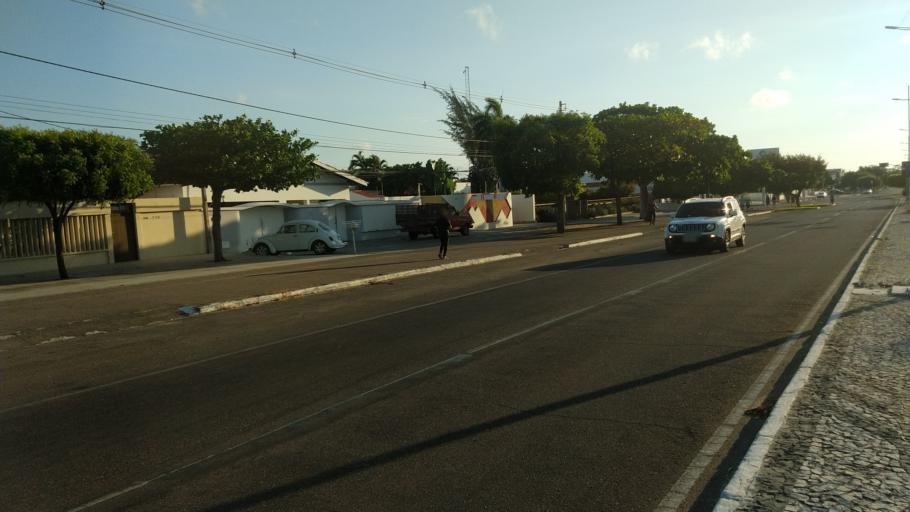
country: BR
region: Bahia
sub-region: Paulo Afonso
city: Paulo Afonso
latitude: -9.3984
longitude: -38.2258
